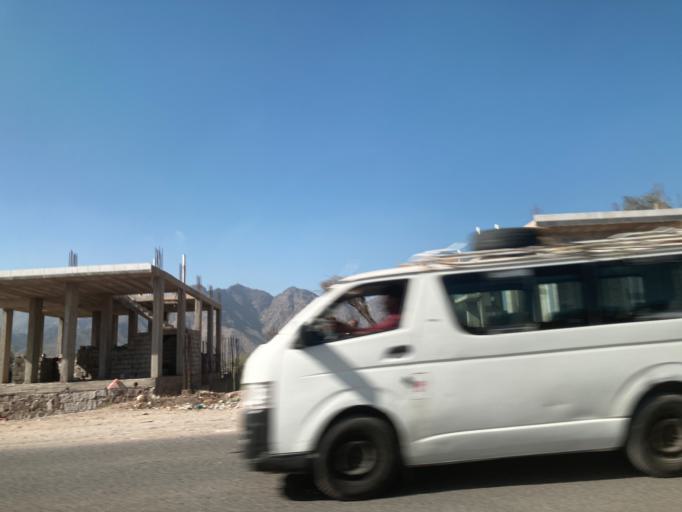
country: YE
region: Ad Dali'
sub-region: Qa'atabah
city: Qa`tabah
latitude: 13.8169
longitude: 44.7157
